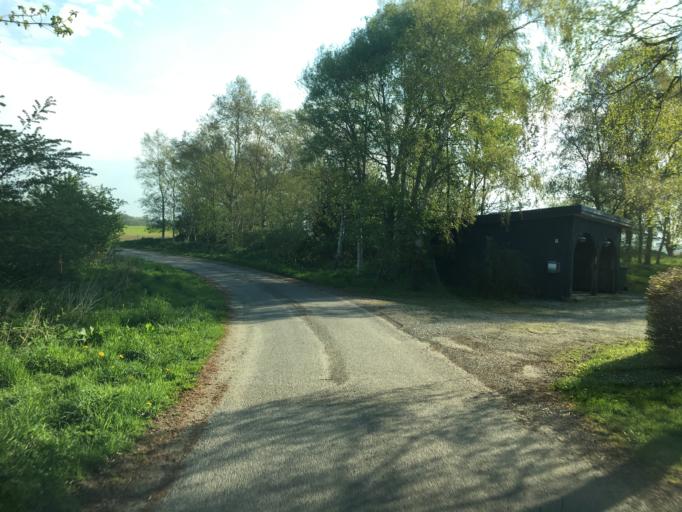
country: DK
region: South Denmark
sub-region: Aabenraa Kommune
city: Rodekro
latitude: 55.1484
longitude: 9.3844
